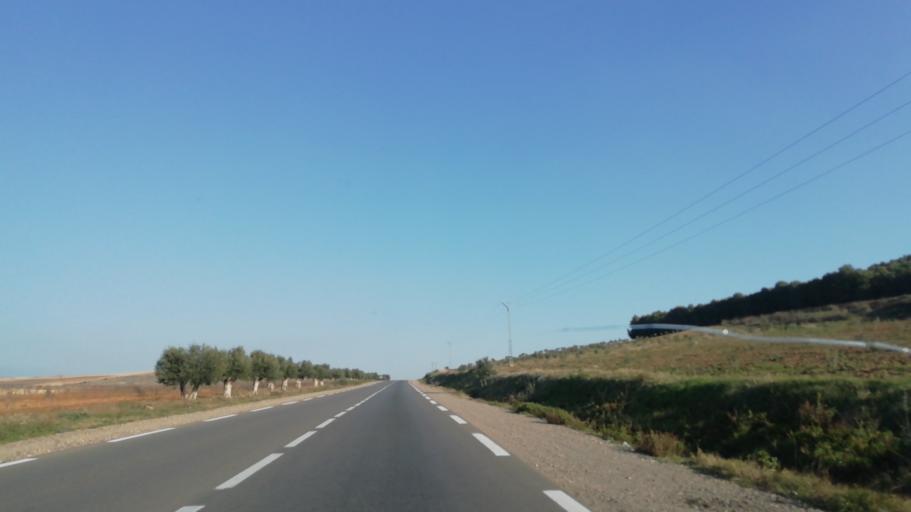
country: DZ
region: Ain Temouchent
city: Hammam Bou Hadjar
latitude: 35.1654
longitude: -0.8818
